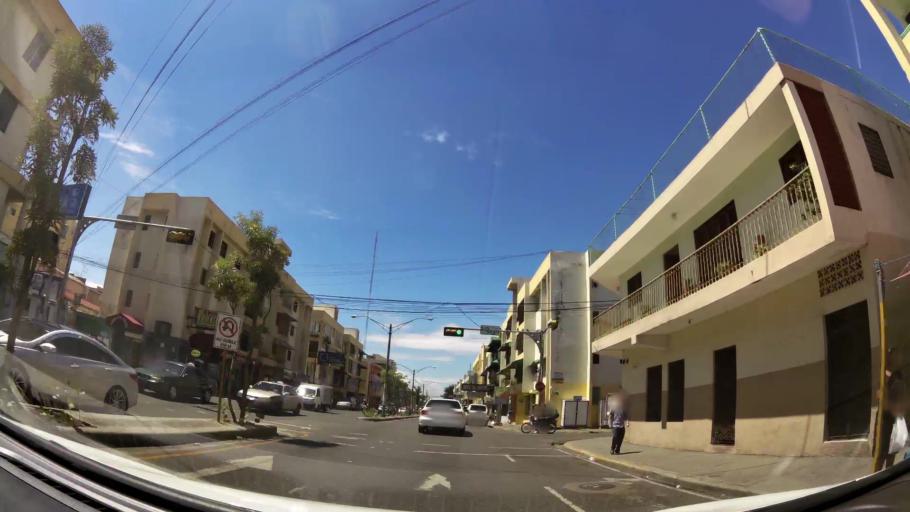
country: DO
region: Santiago
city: Santiago de los Caballeros
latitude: 19.4543
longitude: -70.7012
